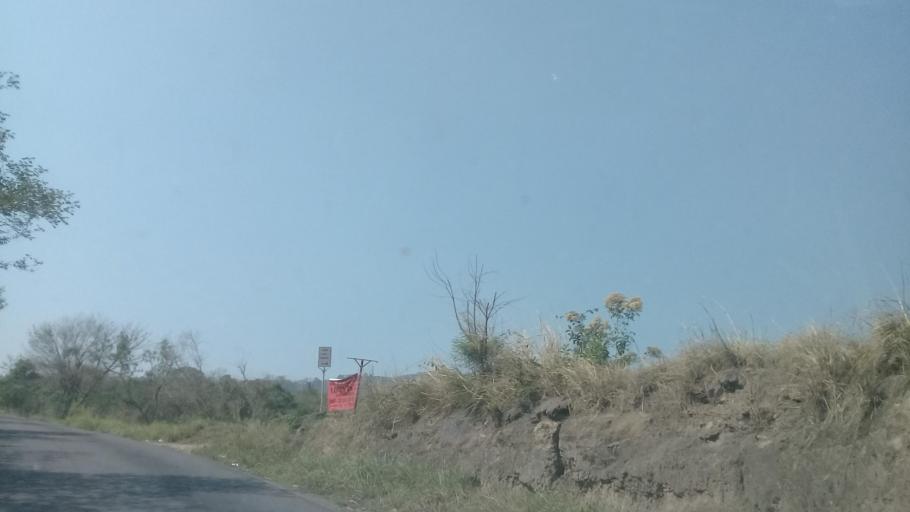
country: MX
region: Veracruz
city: El Castillo
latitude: 19.5758
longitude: -96.8324
